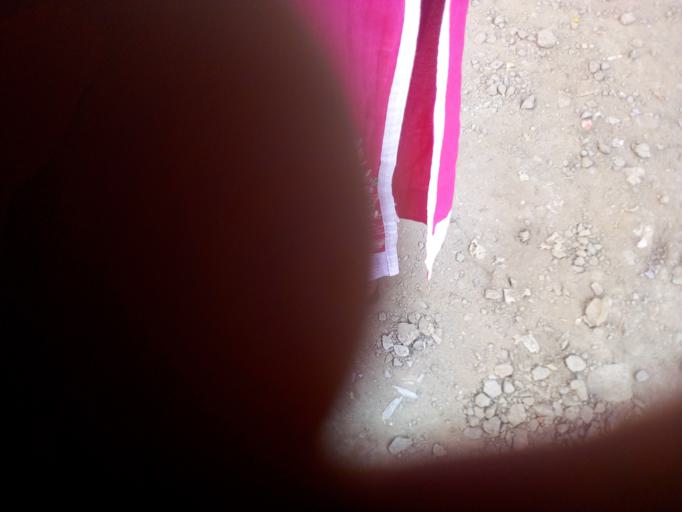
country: IN
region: Maharashtra
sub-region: Solapur
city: Sangola
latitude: 17.4345
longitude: 75.1884
